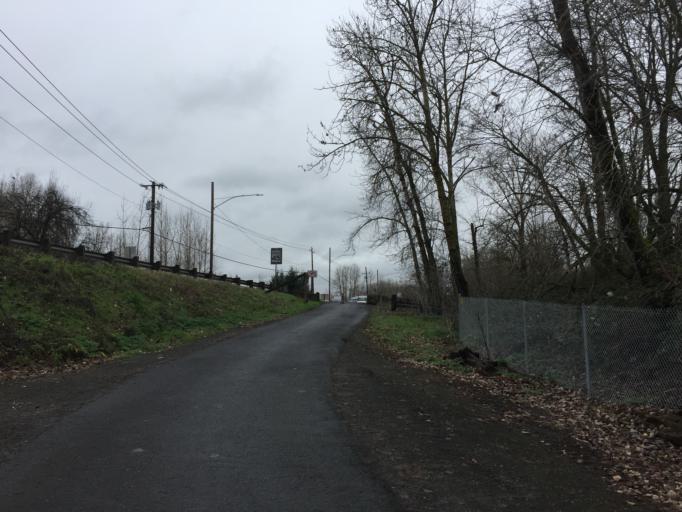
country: US
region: Washington
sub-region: Clark County
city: Vancouver
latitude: 45.6006
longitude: -122.7188
